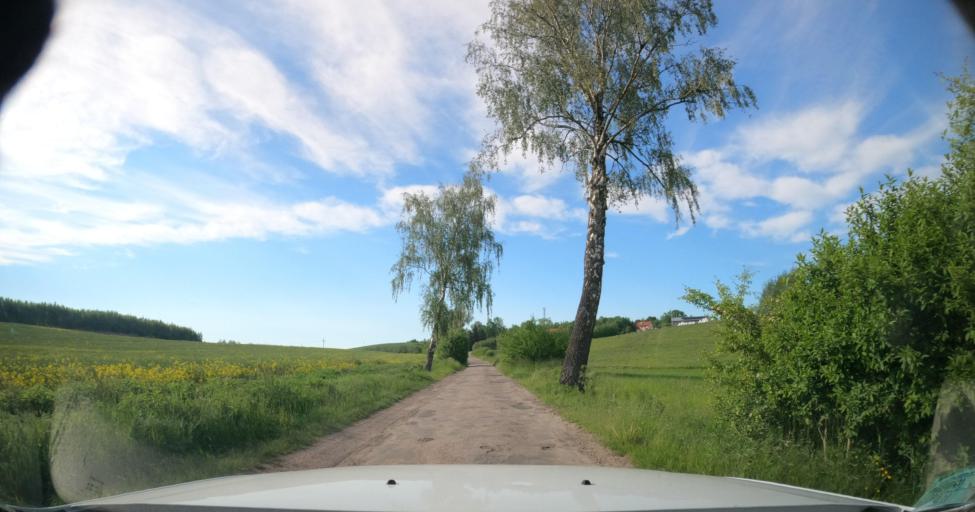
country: PL
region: Warmian-Masurian Voivodeship
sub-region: Powiat ostrodzki
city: Morag
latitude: 54.0576
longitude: 19.8883
